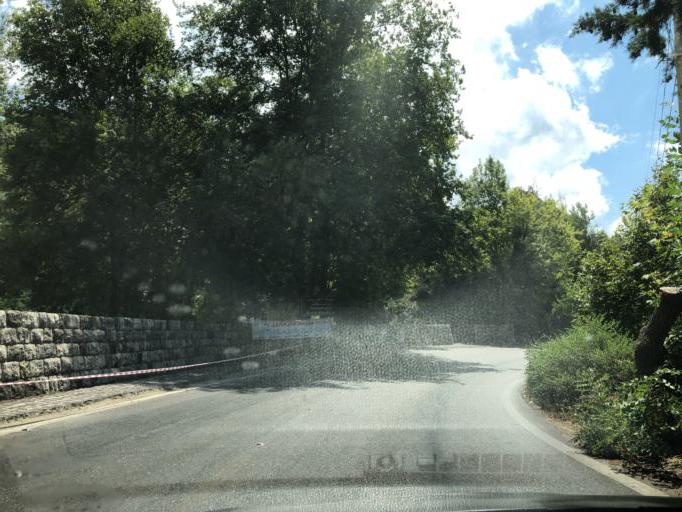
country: LB
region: Mont-Liban
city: Beit ed Dine
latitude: 33.6969
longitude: 35.5882
